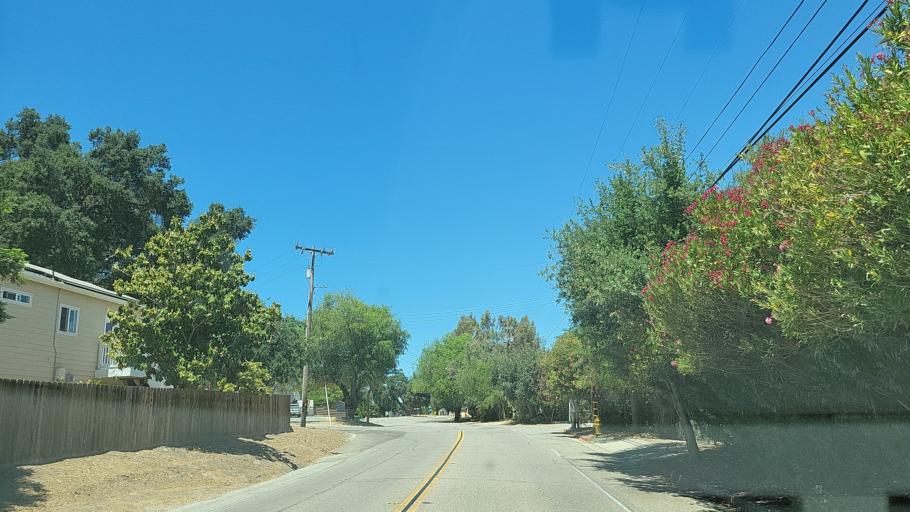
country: US
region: California
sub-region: San Luis Obispo County
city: Atascadero
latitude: 35.5076
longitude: -120.6682
